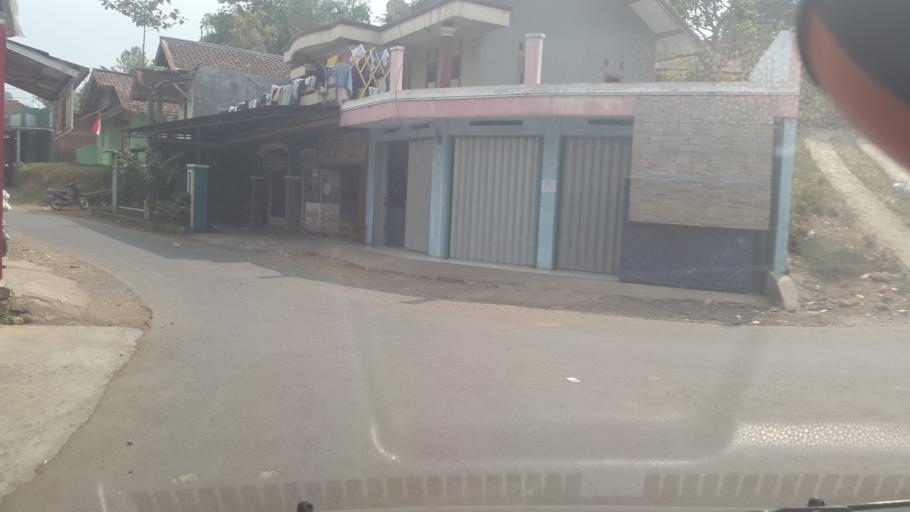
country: ID
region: West Java
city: Nyalindung
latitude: -7.0432
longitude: 106.9379
